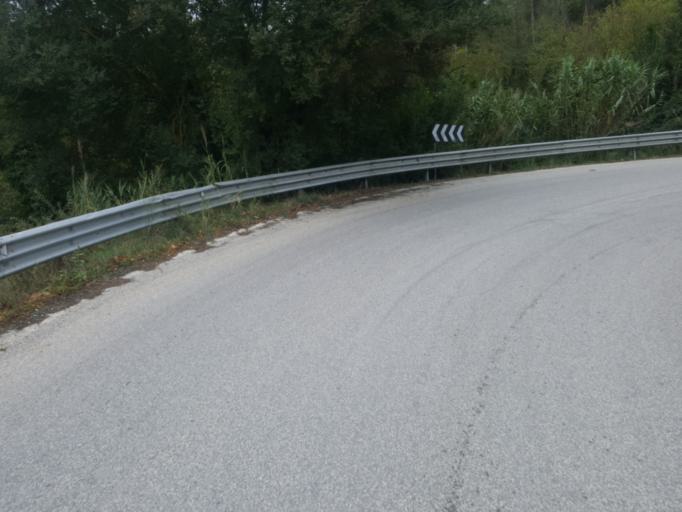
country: IT
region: Tuscany
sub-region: Province of Pisa
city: Saline
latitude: 43.3577
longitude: 10.8147
